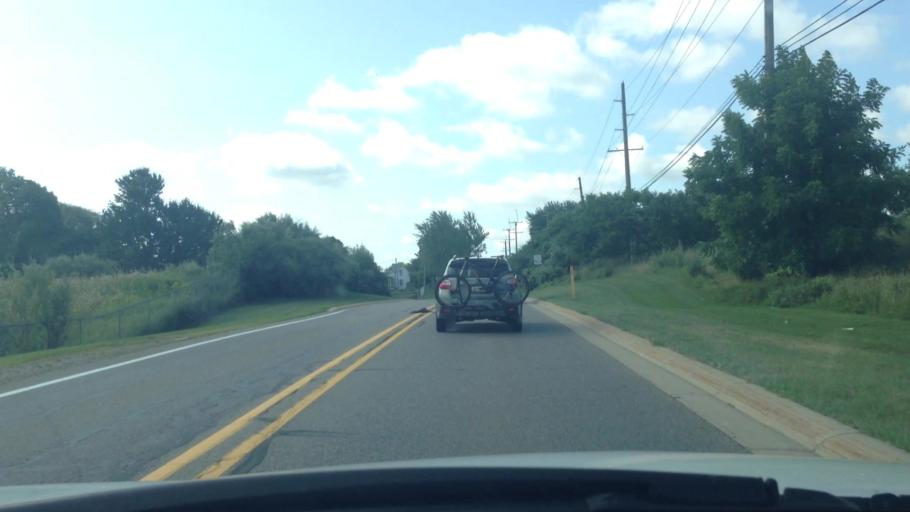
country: US
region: Michigan
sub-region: Oakland County
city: Waterford
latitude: 42.6299
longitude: -83.4427
